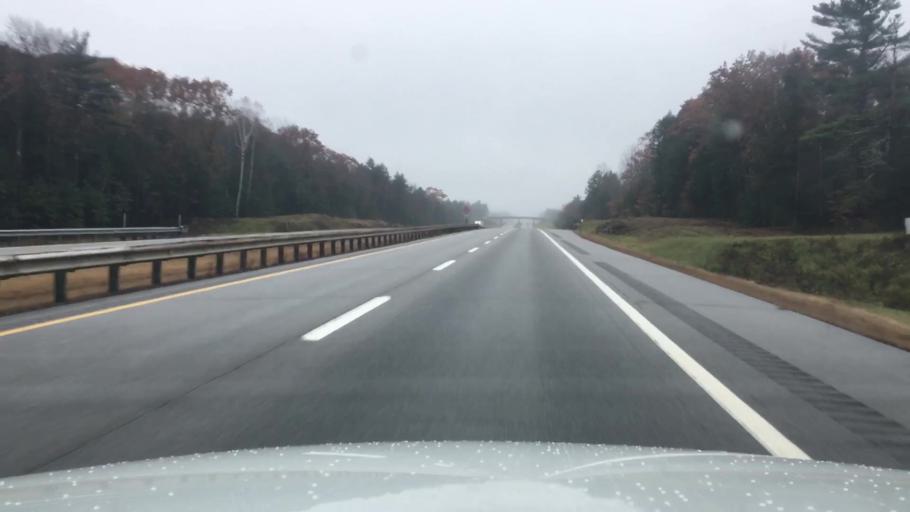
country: US
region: Maine
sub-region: Sagadahoc County
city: Richmond
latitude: 44.1531
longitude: -69.9058
